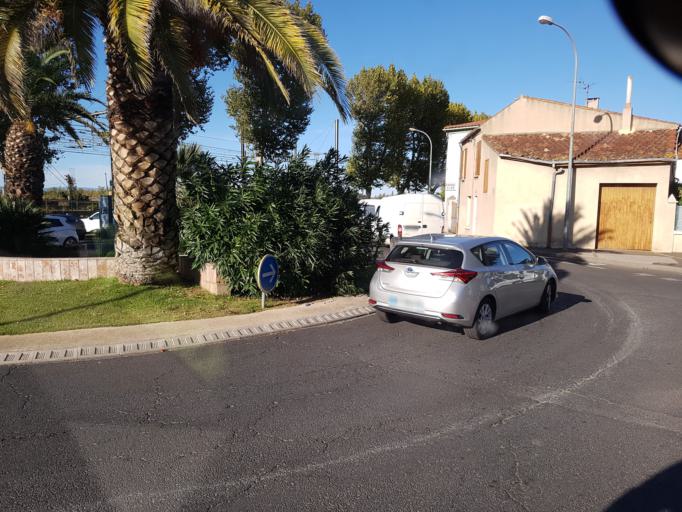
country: FR
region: Languedoc-Roussillon
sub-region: Departement de l'Aude
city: Narbonne
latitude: 43.1936
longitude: 3.0097
